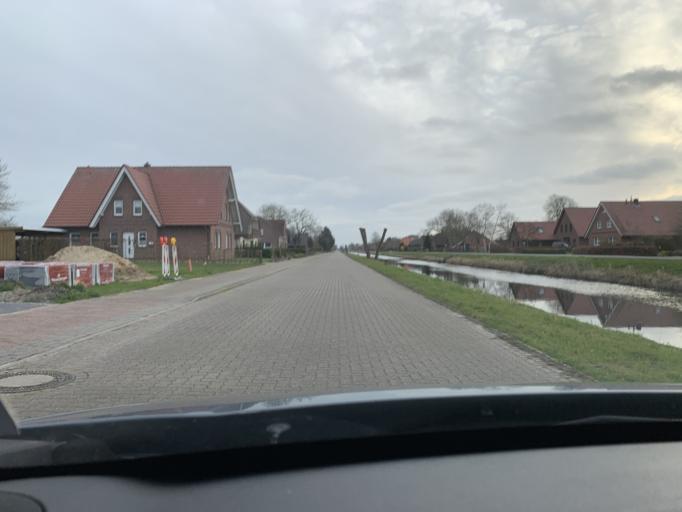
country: DE
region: Lower Saxony
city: Schwerinsdorf
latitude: 53.2770
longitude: 7.7054
